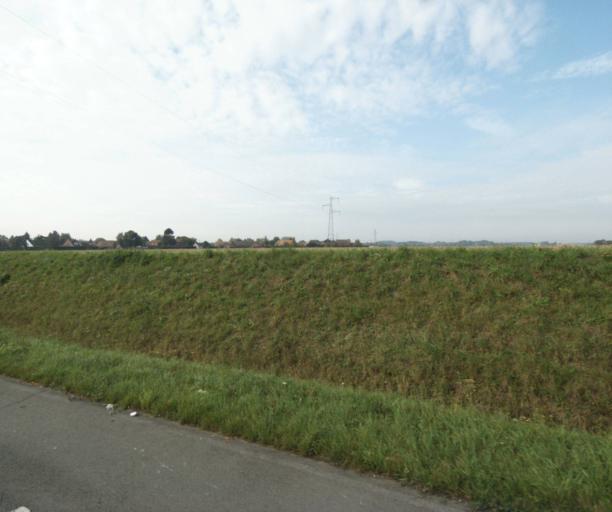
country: FR
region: Nord-Pas-de-Calais
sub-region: Departement du Nord
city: Wattignies
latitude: 50.5870
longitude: 3.0342
